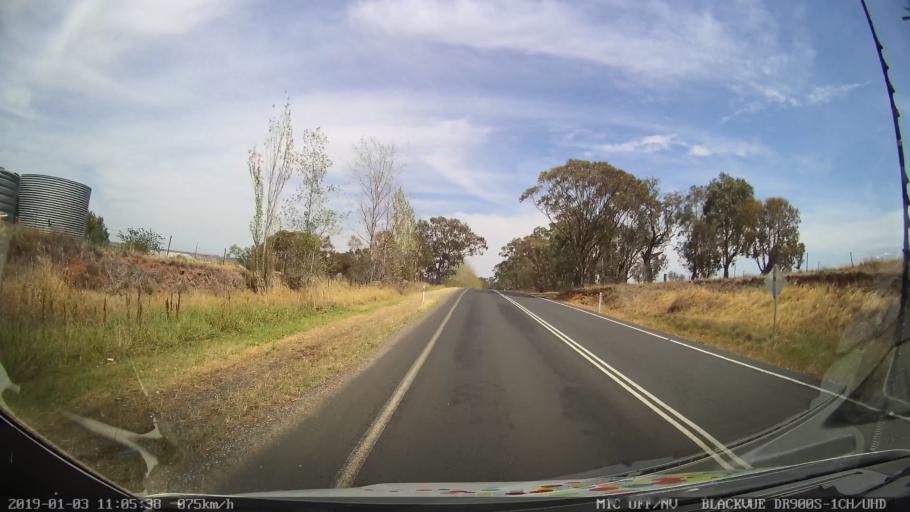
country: AU
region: New South Wales
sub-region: Young
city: Young
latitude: -34.2704
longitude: 148.2828
